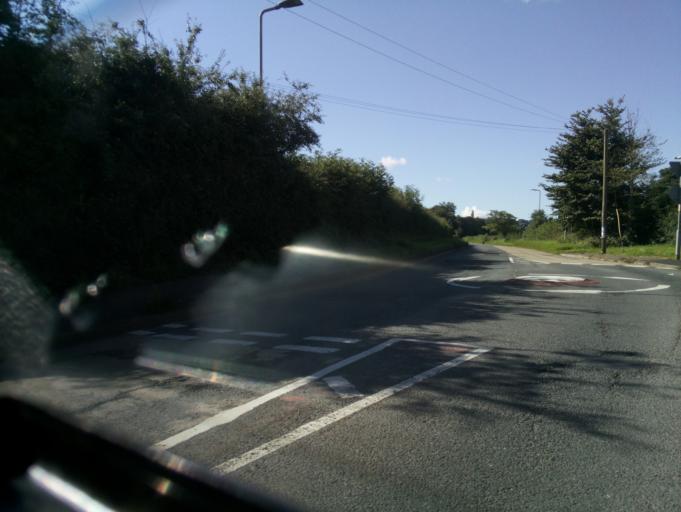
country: GB
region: England
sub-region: Herefordshire
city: Walford
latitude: 51.9007
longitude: -2.5904
